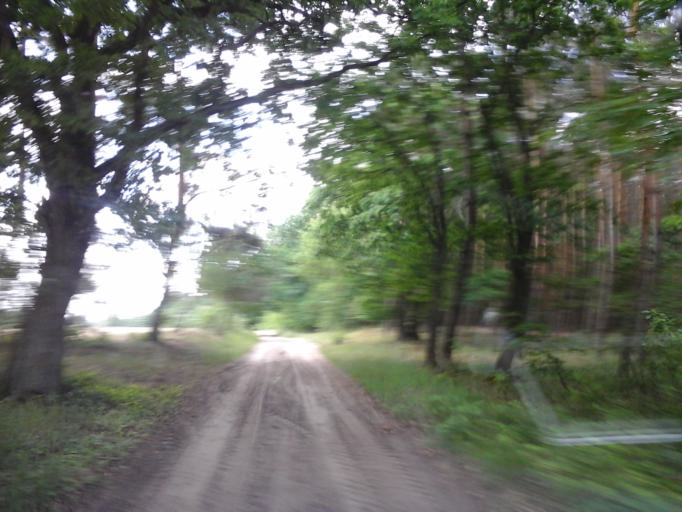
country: PL
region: Lubusz
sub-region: Powiat strzelecko-drezdenecki
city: Dobiegniew
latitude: 53.0584
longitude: 15.7626
